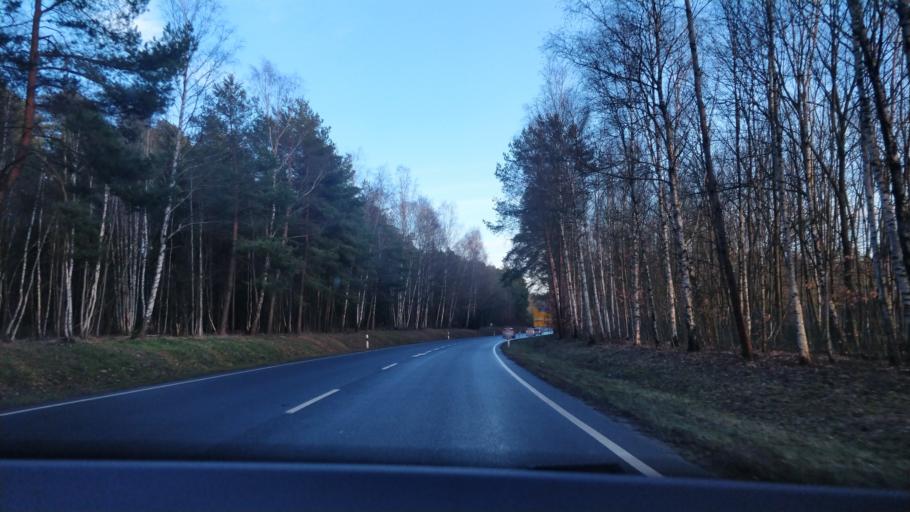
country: DE
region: Bavaria
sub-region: Upper Palatinate
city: Parkstein
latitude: 49.6893
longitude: 12.1017
